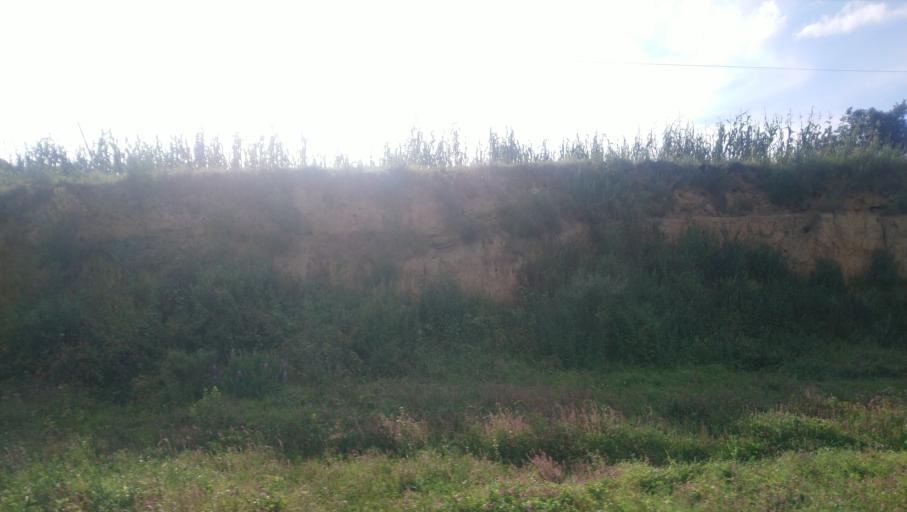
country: MX
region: Mexico
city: Juchitepec de Mariano Riva Palacio
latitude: 19.1330
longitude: -98.9349
